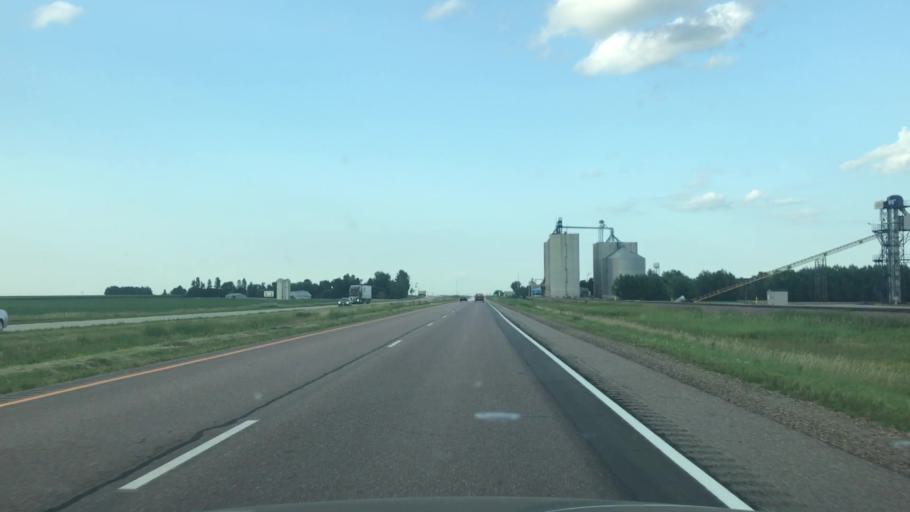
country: US
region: Minnesota
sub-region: Nobles County
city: Worthington
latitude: 43.6938
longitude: -95.4789
